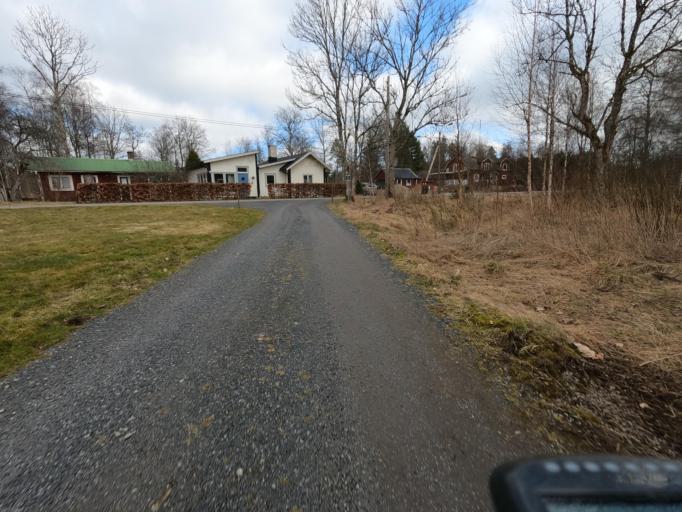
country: SE
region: Kronoberg
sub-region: Alvesta Kommun
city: Vislanda
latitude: 56.8166
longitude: 14.3732
